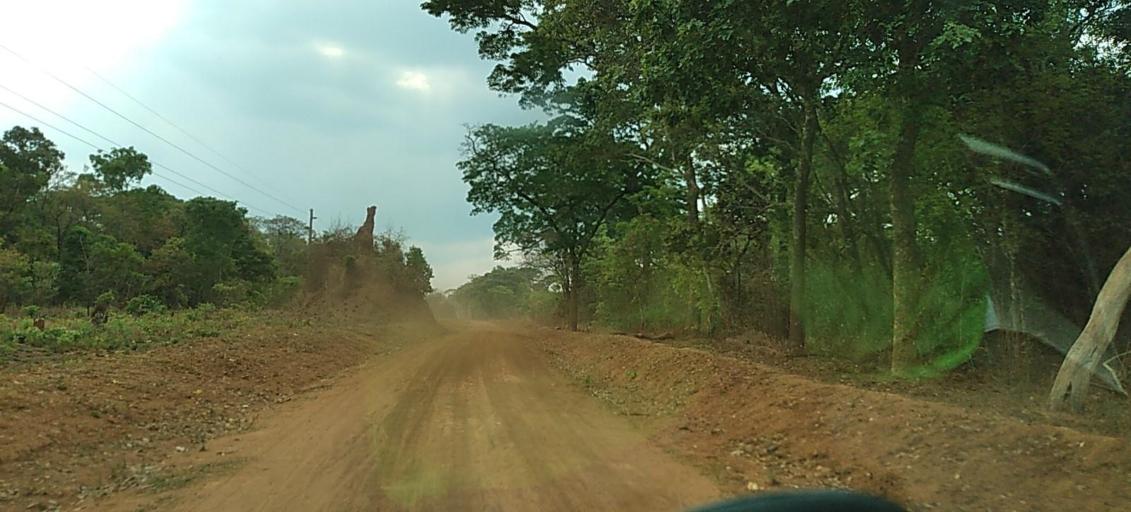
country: ZM
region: North-Western
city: Solwezi
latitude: -12.7846
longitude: 26.5047
